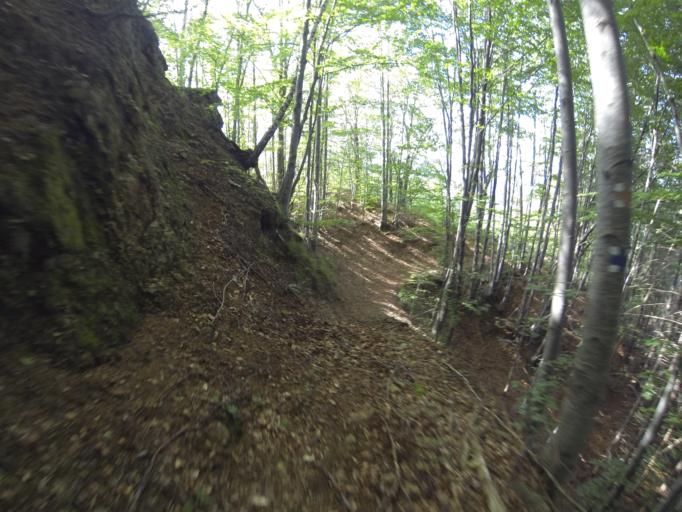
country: RO
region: Valcea
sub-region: Comuna Barbatesti
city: Barbatesti
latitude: 45.2569
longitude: 24.1546
